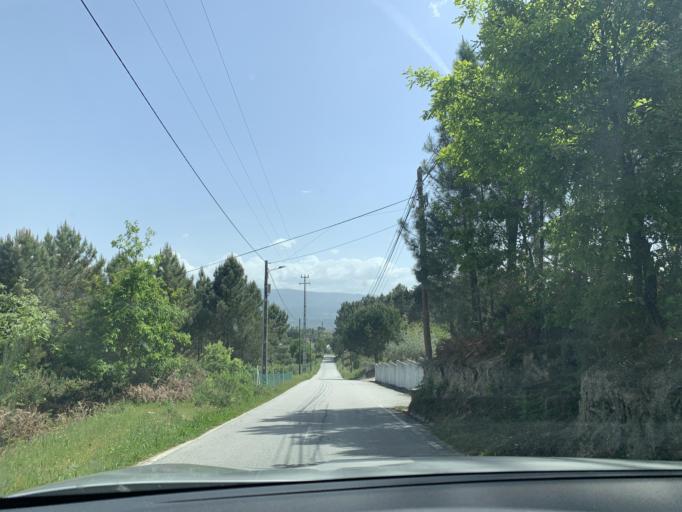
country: PT
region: Guarda
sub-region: Fornos de Algodres
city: Fornos de Algodres
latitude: 40.5943
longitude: -7.6301
